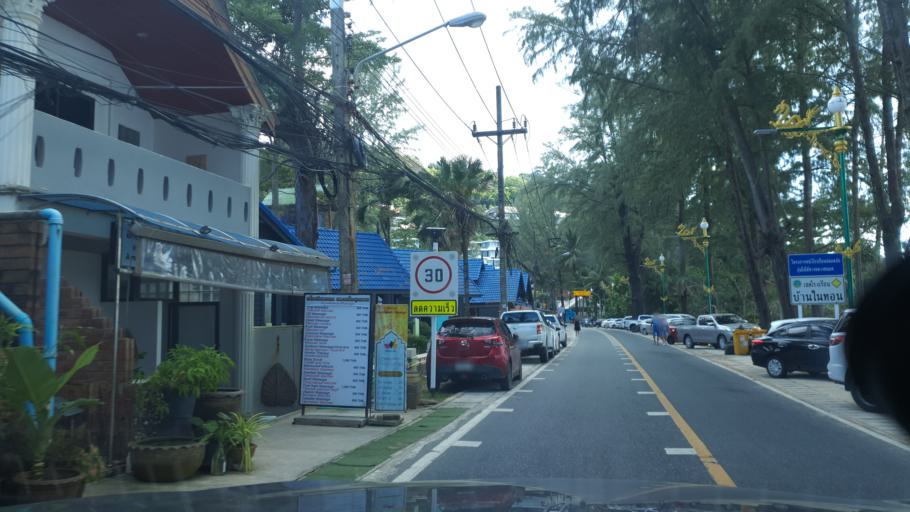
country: TH
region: Phuket
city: Thalang
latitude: 8.0577
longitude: 98.2782
